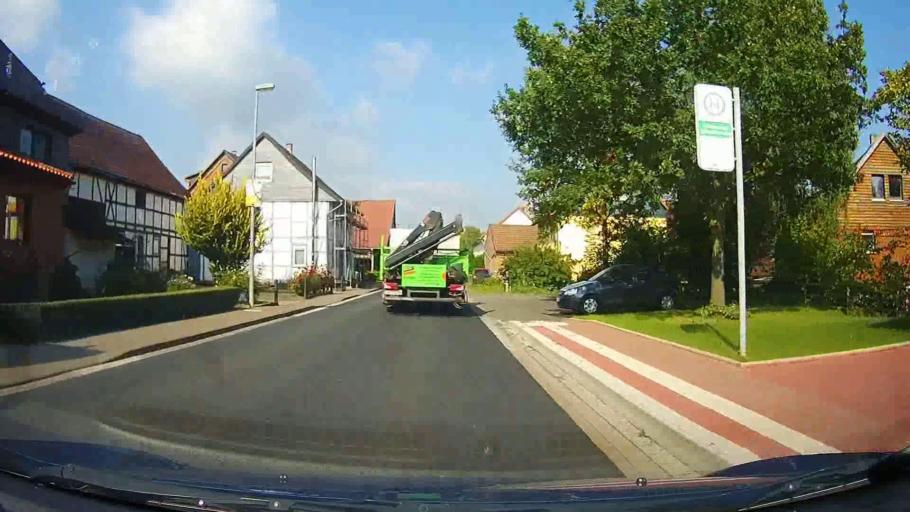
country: DE
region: Lower Saxony
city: Hardegsen
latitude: 51.6629
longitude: 9.8465
